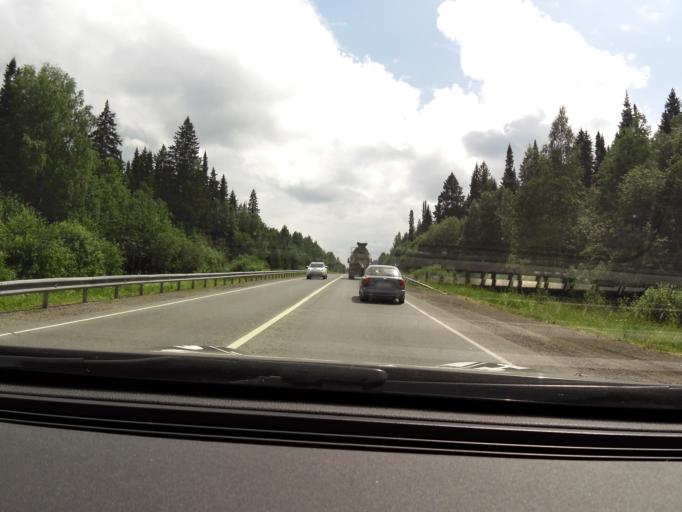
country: RU
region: Perm
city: Kungur
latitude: 57.3230
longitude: 56.9626
